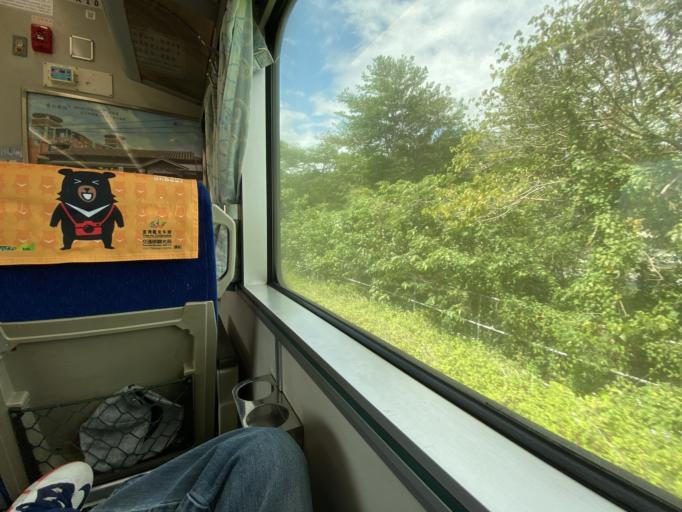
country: TW
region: Taiwan
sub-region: Taitung
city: Taitung
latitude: 22.9049
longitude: 121.1377
